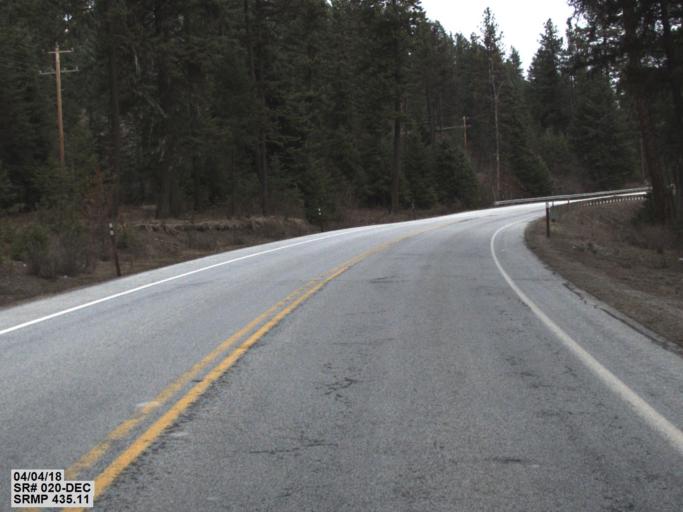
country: US
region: Washington
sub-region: Pend Oreille County
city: Newport
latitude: 48.2049
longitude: -117.0647
